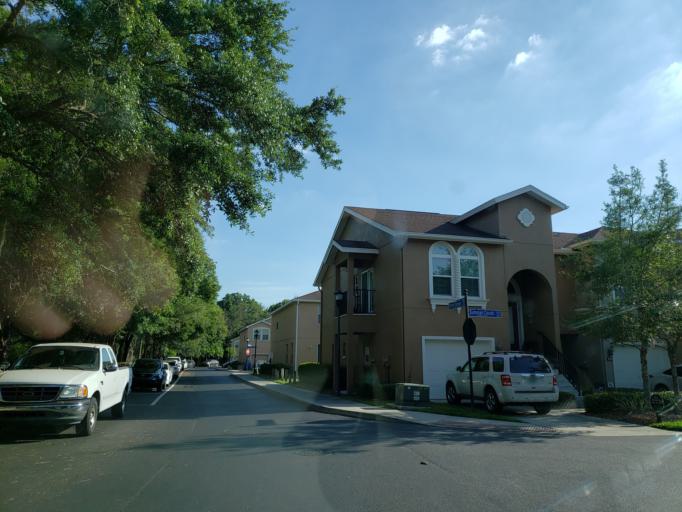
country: US
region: Florida
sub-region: Hillsborough County
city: Brandon
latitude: 27.9291
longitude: -82.2891
